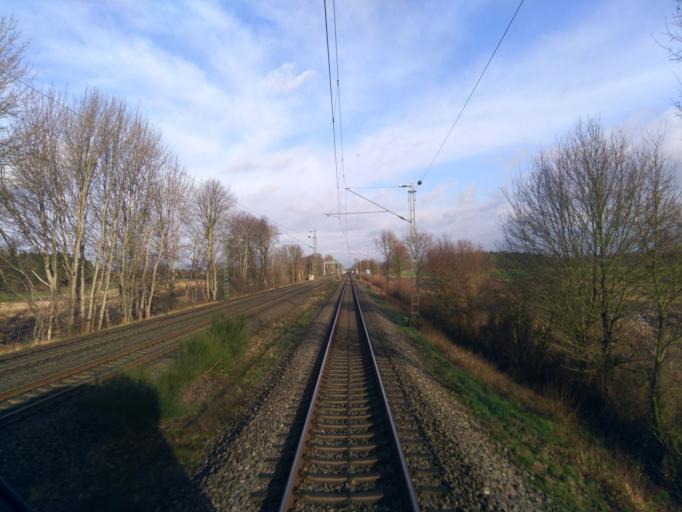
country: DE
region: Lower Saxony
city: Scheessel
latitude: 53.1494
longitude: 9.4749
